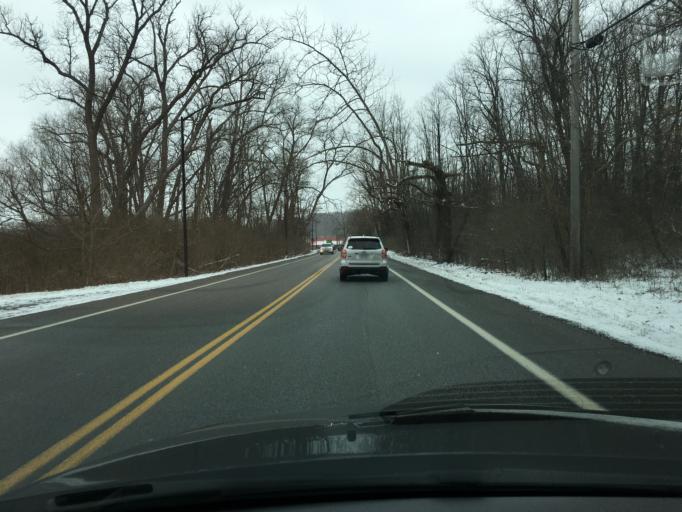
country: US
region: Ohio
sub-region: Summit County
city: Fairlawn
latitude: 41.1367
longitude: -81.5579
